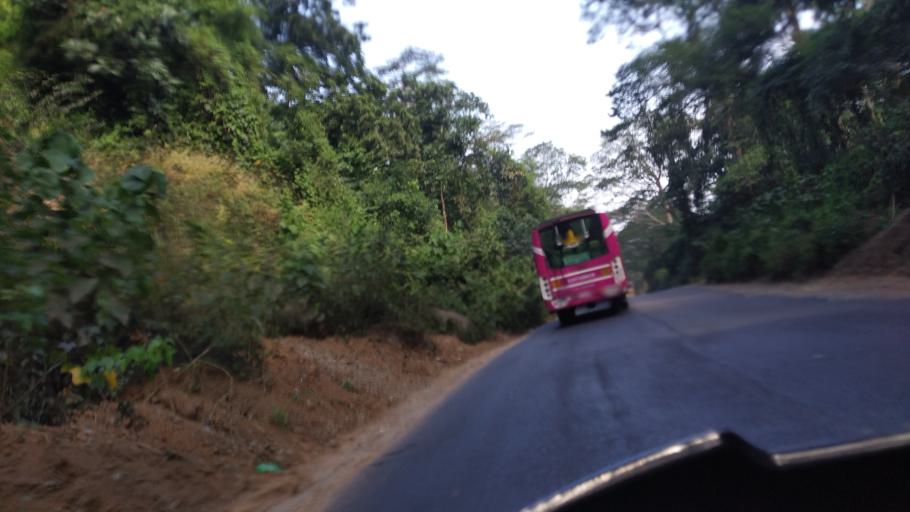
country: IN
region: Kerala
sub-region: Thrissur District
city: Chelakara
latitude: 10.5769
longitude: 76.3801
